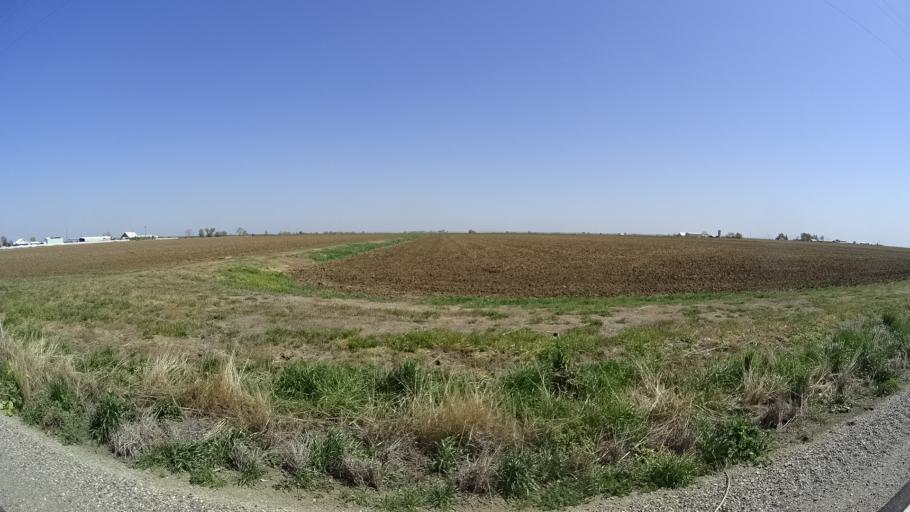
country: US
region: California
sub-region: Glenn County
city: Willows
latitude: 39.4994
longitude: -122.1368
